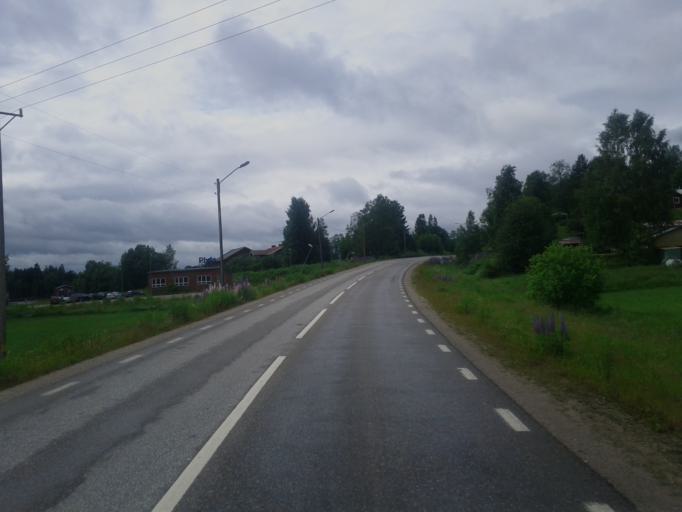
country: SE
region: Gaevleborg
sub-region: Hudiksvalls Kommun
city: Delsbo
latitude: 62.1005
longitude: 16.7264
